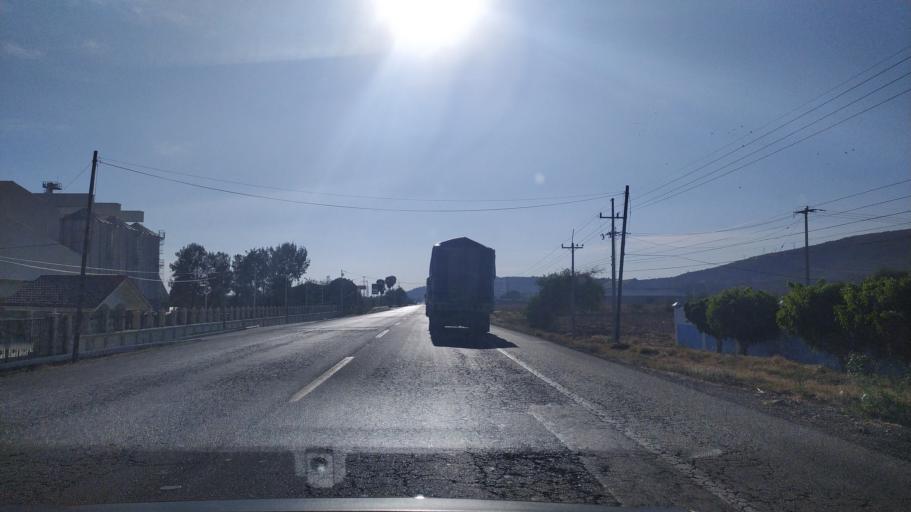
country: MX
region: Jalisco
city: Jamay
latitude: 20.2943
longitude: -102.6795
